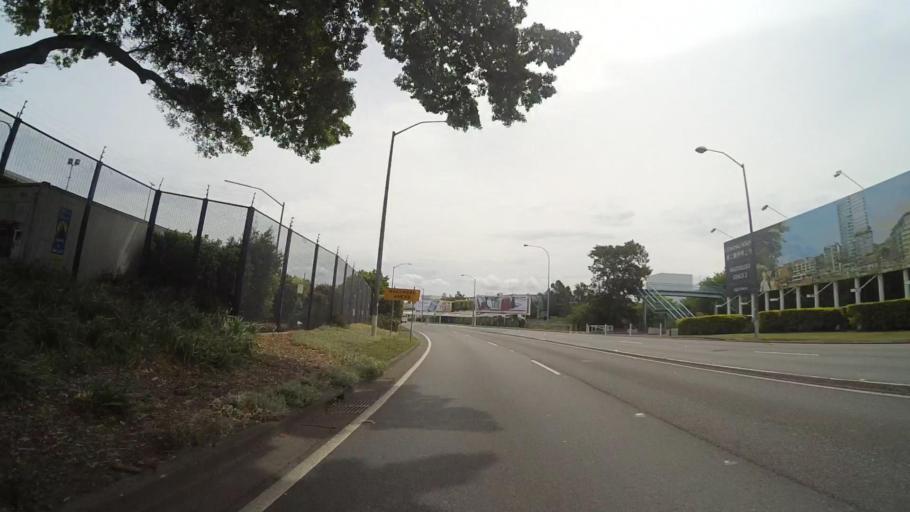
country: AU
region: New South Wales
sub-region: Botany Bay
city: Mascot
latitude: -33.9259
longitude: 151.1794
